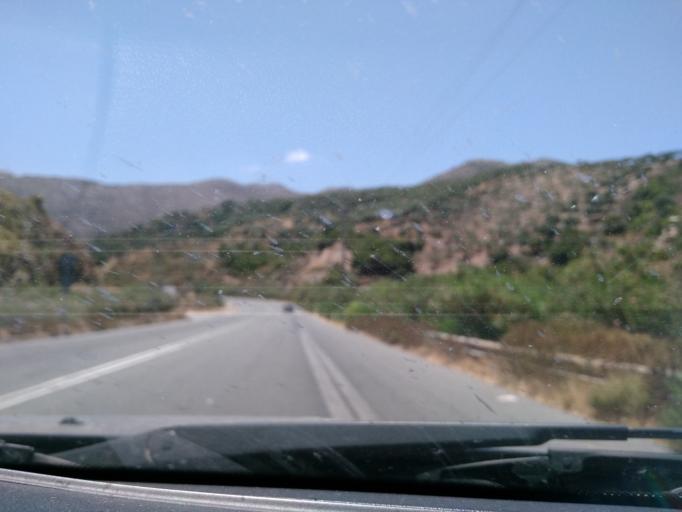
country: GR
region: Crete
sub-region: Nomos Rethymnis
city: Anogeia
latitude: 35.3932
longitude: 24.9217
